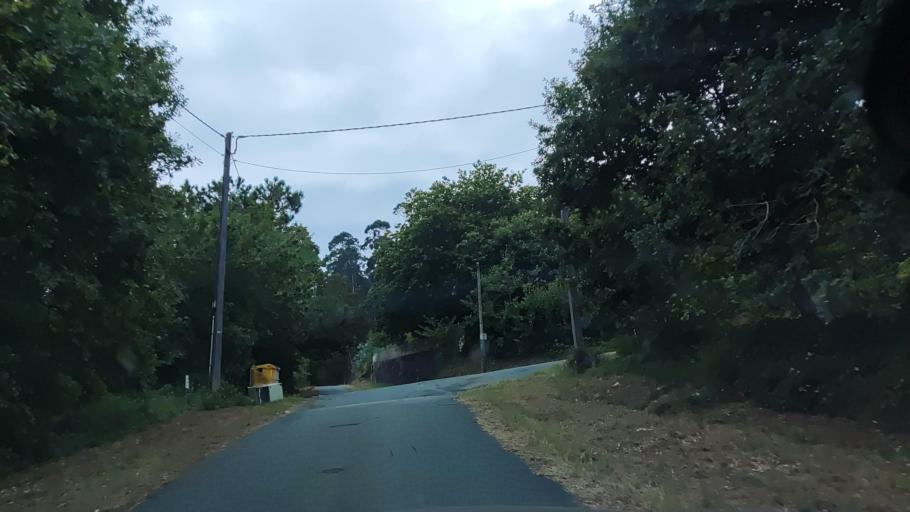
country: ES
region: Galicia
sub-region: Provincia de Pontevedra
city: Catoira
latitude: 42.7044
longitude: -8.7242
